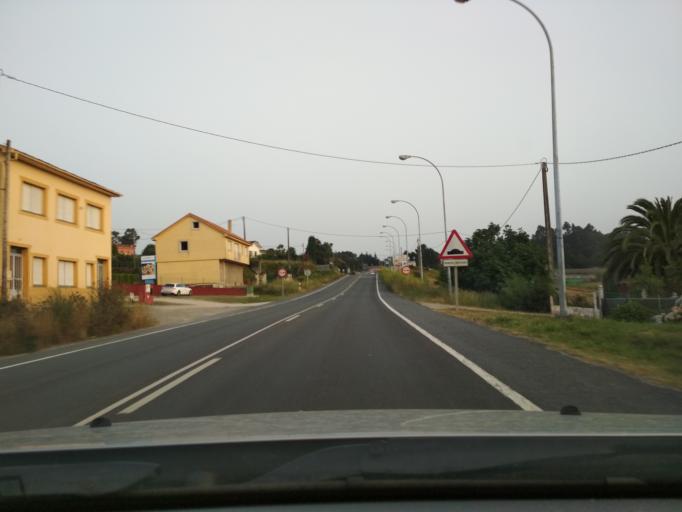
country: ES
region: Galicia
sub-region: Provincia da Coruna
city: Cambre
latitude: 43.2790
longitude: -8.3656
